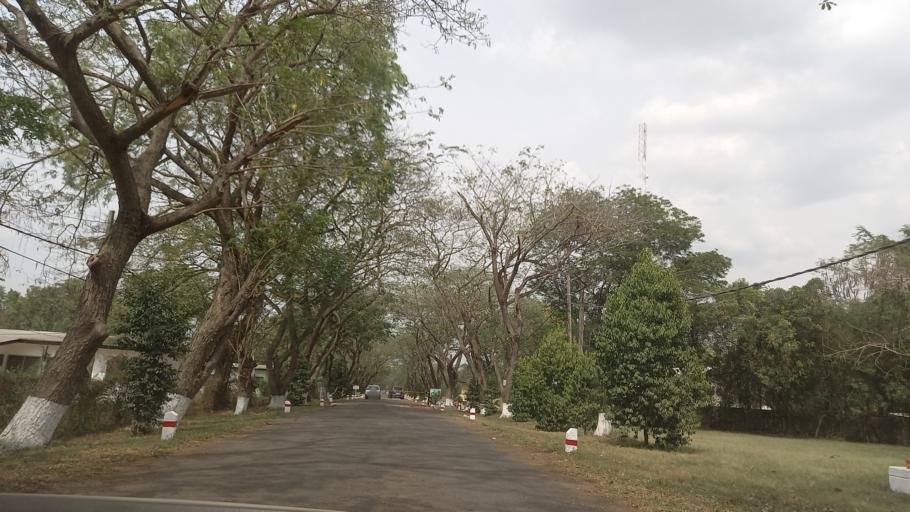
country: GH
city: Akropong
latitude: 6.0924
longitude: 0.1134
